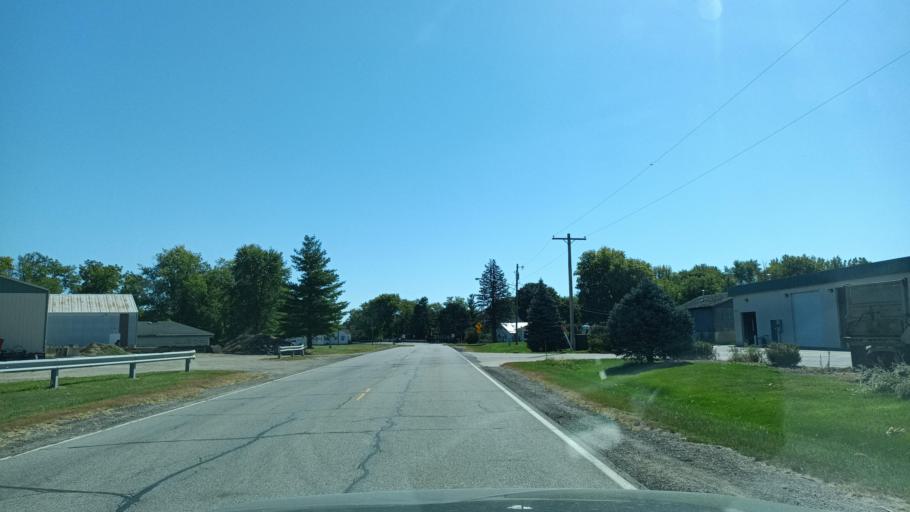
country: US
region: Illinois
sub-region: Peoria County
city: Elmwood
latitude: 40.8399
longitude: -89.8916
